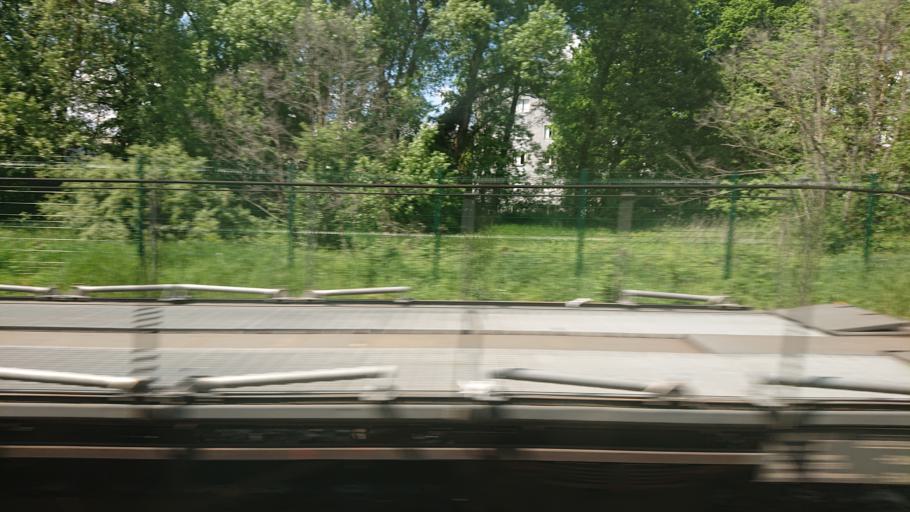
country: FR
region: Rhone-Alpes
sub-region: Departement de l'Ain
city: Montluel
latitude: 45.8455
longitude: 5.0528
